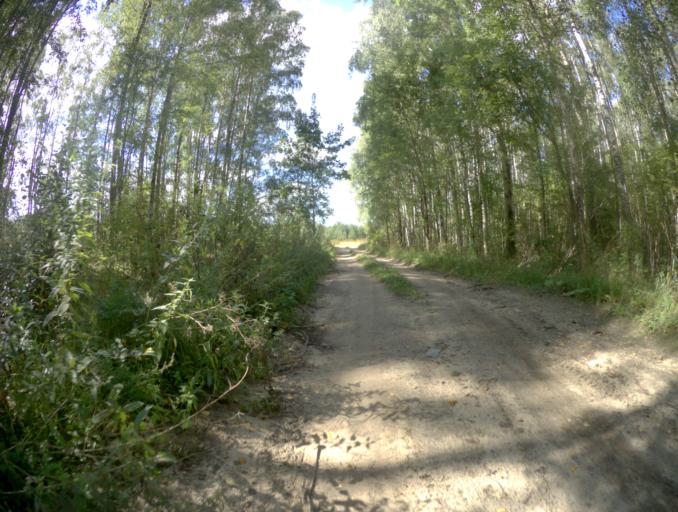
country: RU
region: Vladimir
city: Nikologory
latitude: 56.0178
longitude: 41.9333
